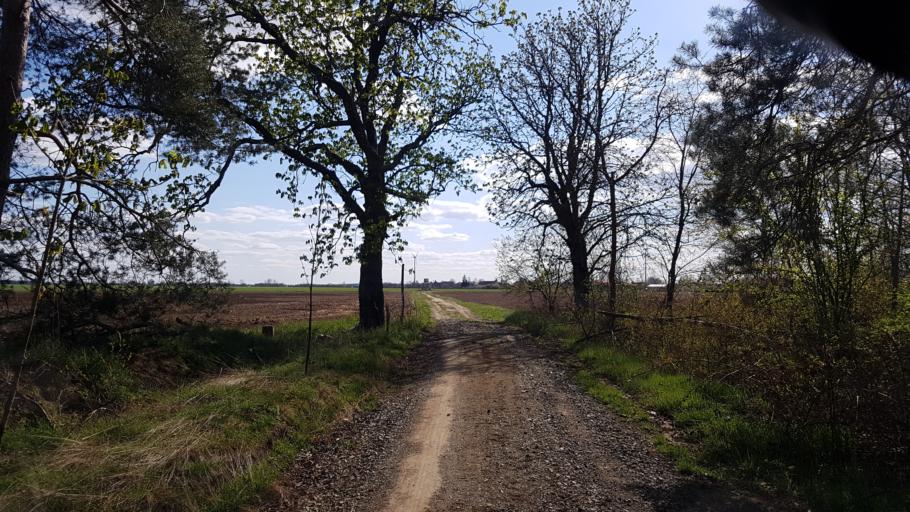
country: DE
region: Brandenburg
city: Muhlberg
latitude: 51.4787
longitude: 13.2783
